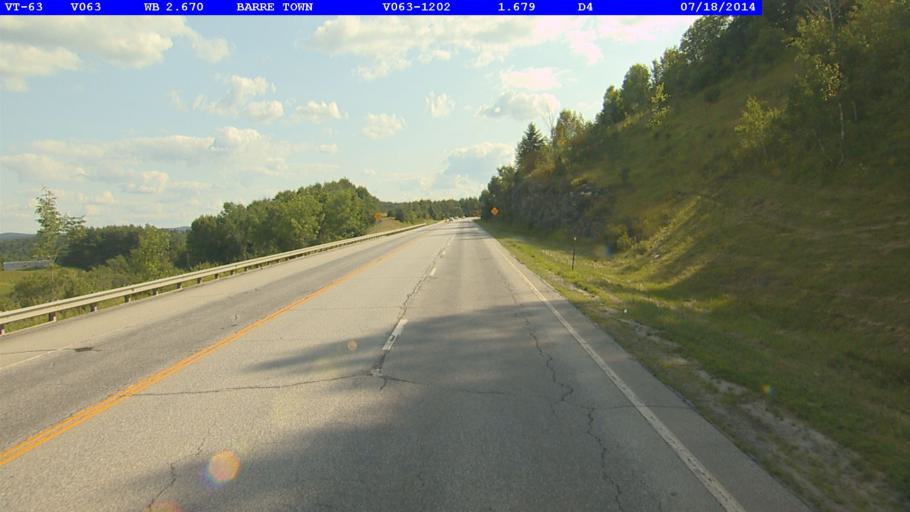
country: US
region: Vermont
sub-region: Washington County
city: South Barre
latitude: 44.1663
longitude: -72.5286
